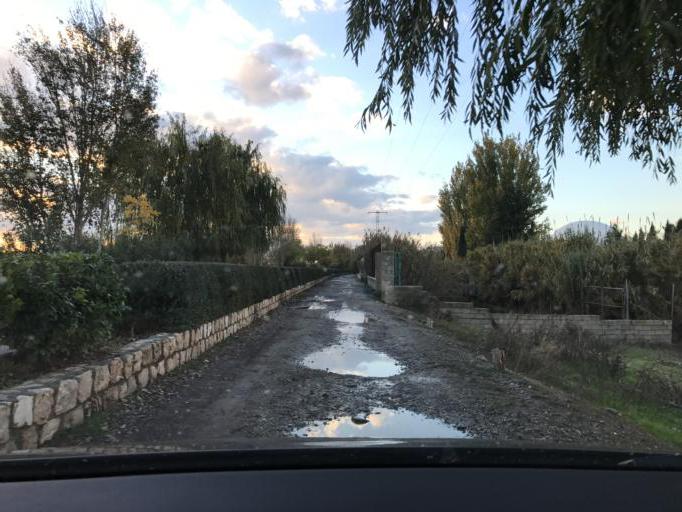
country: ES
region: Andalusia
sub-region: Provincia de Granada
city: Armilla
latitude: 37.1623
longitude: -3.6228
